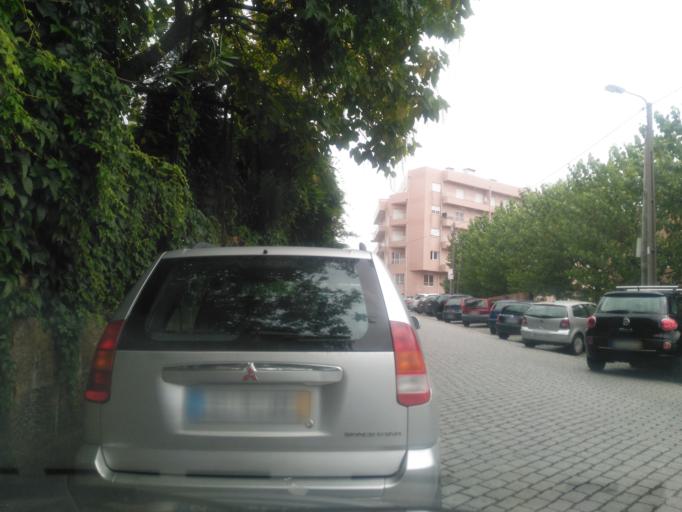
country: PT
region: Braga
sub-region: Braga
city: Braga
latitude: 41.5422
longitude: -8.4343
